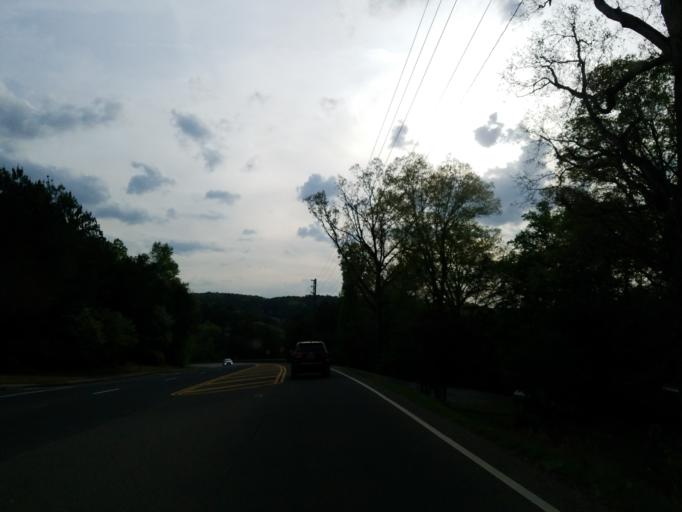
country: US
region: Georgia
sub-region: Cherokee County
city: Canton
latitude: 34.2245
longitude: -84.4783
